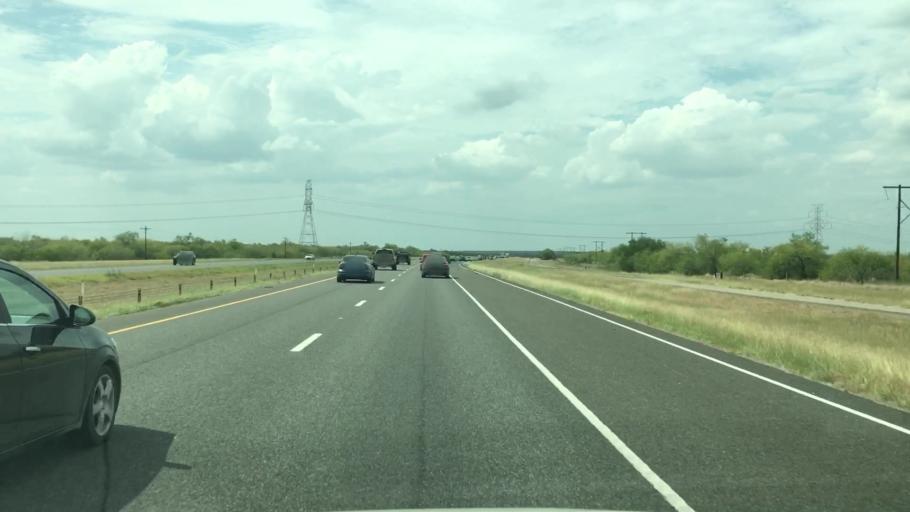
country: US
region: Texas
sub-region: Atascosa County
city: Pleasanton
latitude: 28.8184
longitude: -98.3592
